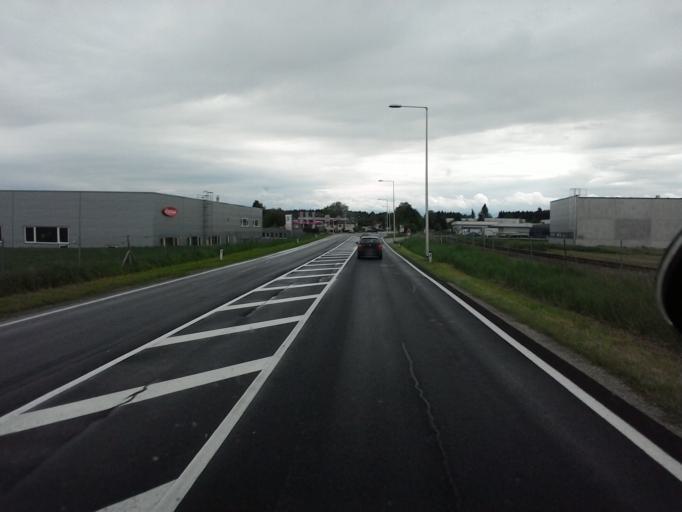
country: AT
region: Upper Austria
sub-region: Wels-Land
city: Steinhaus
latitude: 48.1060
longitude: 14.0390
